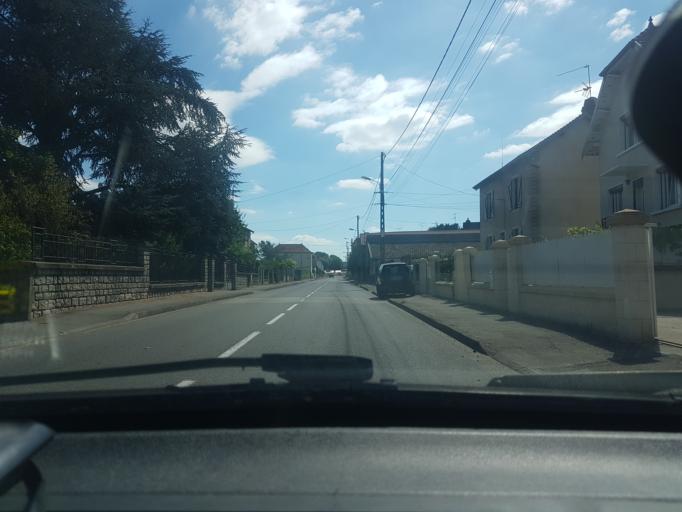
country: FR
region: Franche-Comte
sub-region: Departement de la Haute-Saone
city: Gray
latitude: 47.4435
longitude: 5.5987
